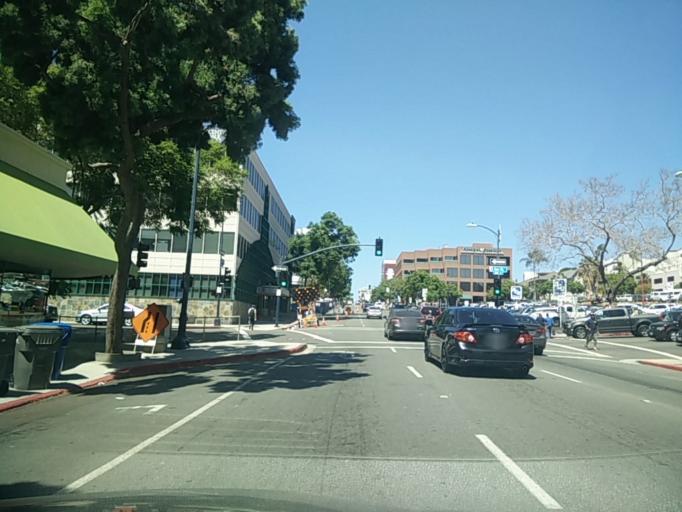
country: US
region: California
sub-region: San Diego County
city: San Diego
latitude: 32.7196
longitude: -117.1602
